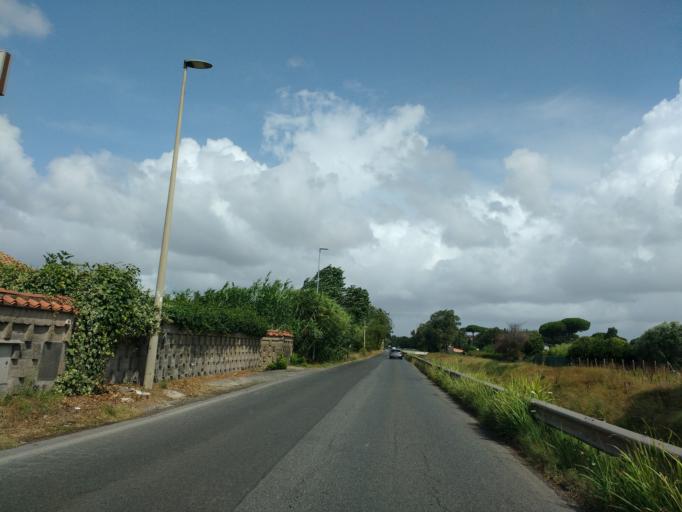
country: IT
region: Latium
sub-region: Citta metropolitana di Roma Capitale
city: Acilia-Castel Fusano-Ostia Antica
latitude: 41.7637
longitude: 12.3273
